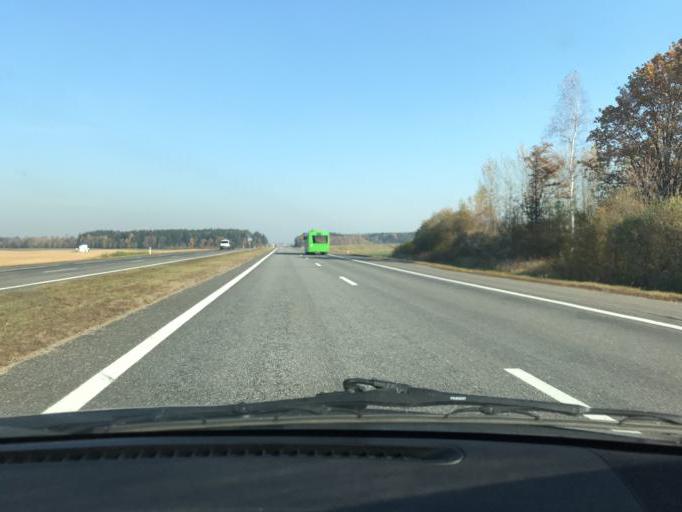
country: BY
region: Vitebsk
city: Horad Orsha
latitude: 54.5796
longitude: 30.3302
